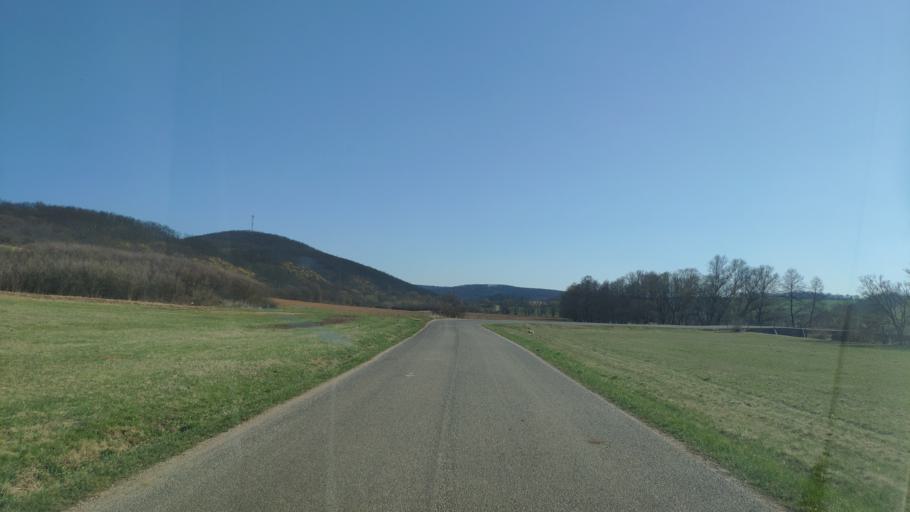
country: SK
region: Banskobystricky
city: Revuca
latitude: 48.5407
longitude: 20.3033
